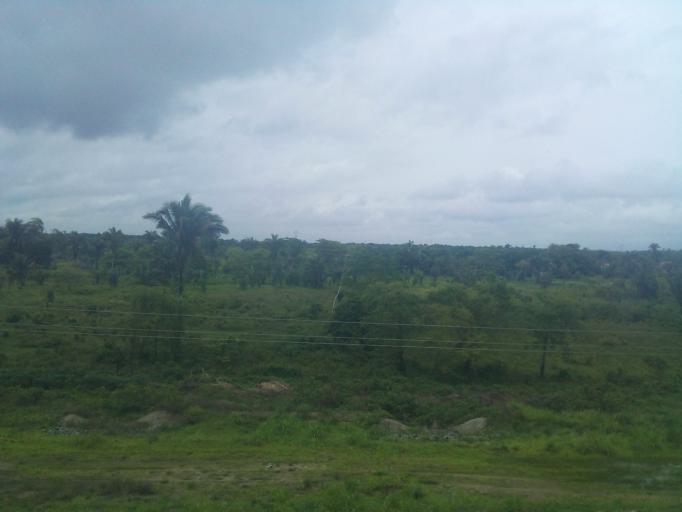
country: BR
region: Maranhao
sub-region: Vitoria Do Mearim
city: Vitoria do Mearim
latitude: -3.5488
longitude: -44.8290
